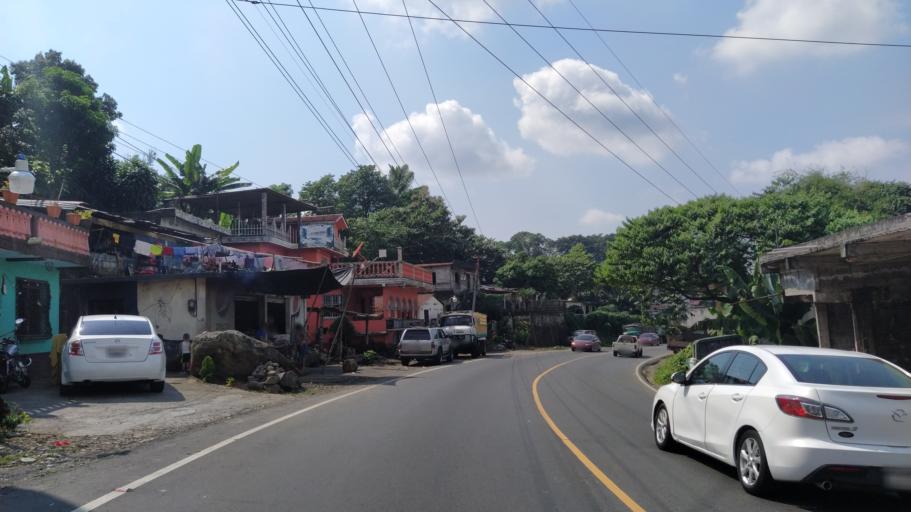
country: GT
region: Quetzaltenango
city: El Palmar
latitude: 14.6349
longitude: -91.5770
